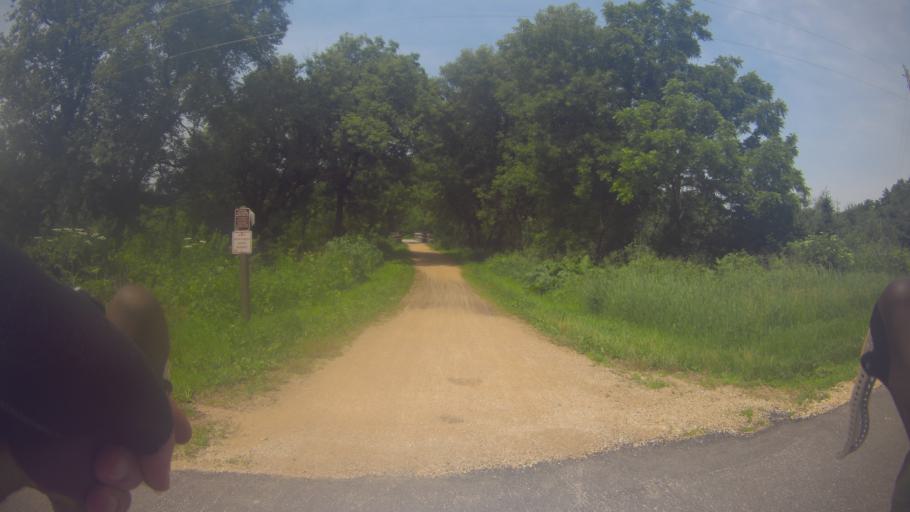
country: US
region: Wisconsin
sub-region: Dane County
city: Mount Horeb
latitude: 43.0163
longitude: -89.6915
